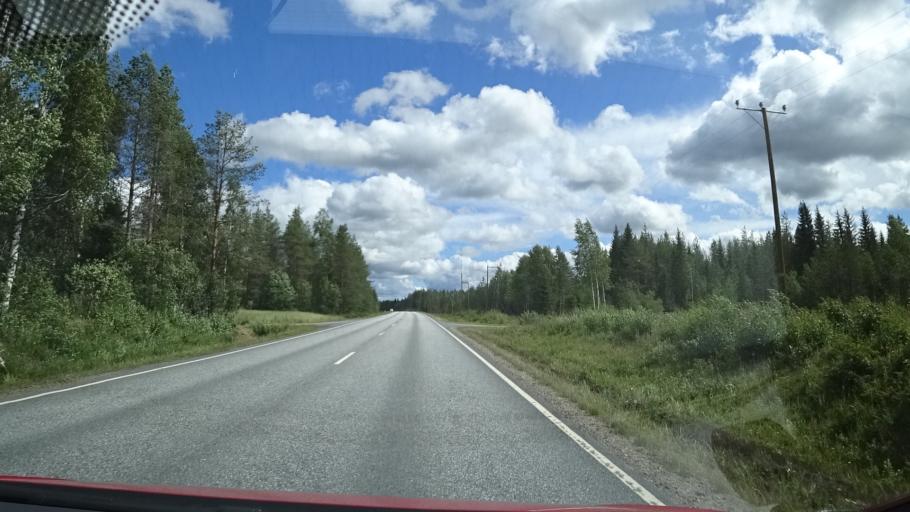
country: FI
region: Northern Savo
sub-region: Koillis-Savo
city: Rautavaara
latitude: 63.3690
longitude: 28.5994
